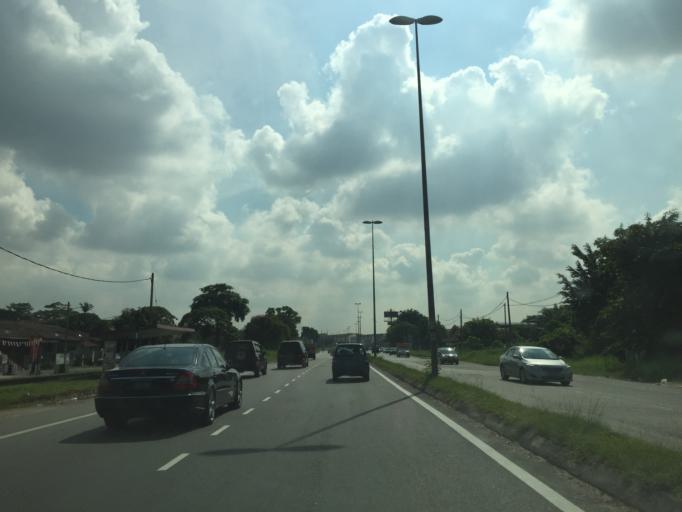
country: MY
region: Selangor
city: Klang
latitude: 3.0122
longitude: 101.4624
